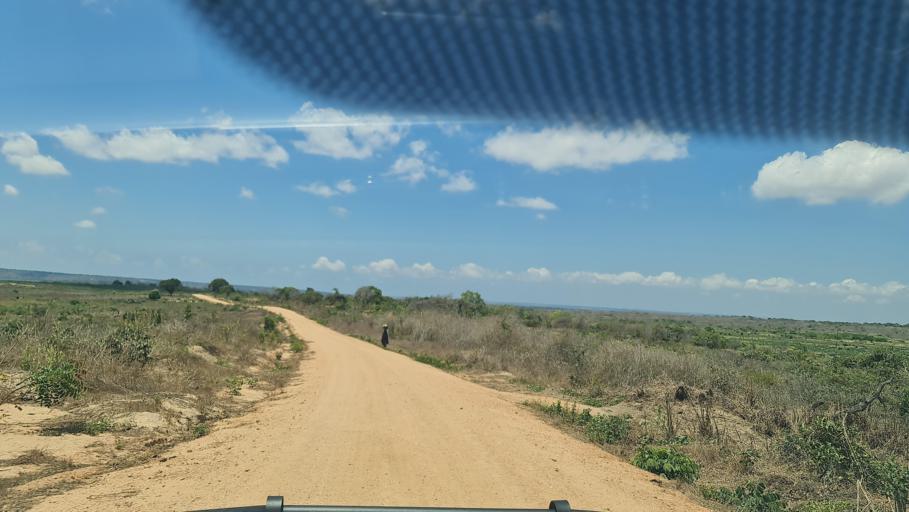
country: MZ
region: Nampula
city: Nacala
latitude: -14.3280
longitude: 40.5918
